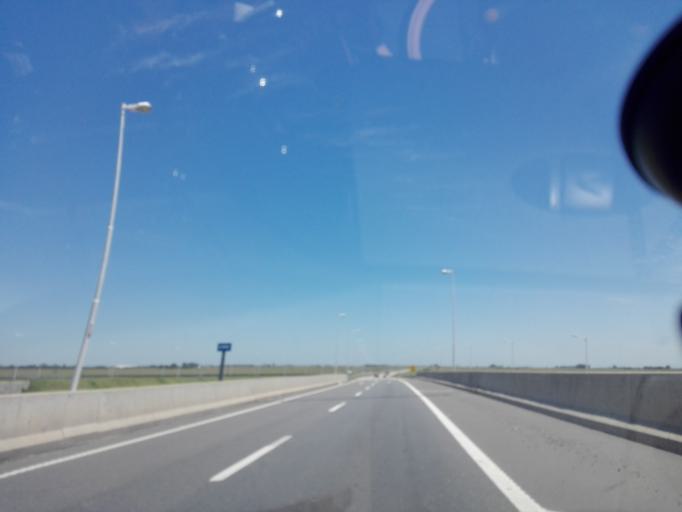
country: AR
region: Cordoba
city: Leones
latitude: -32.6372
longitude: -62.2479
